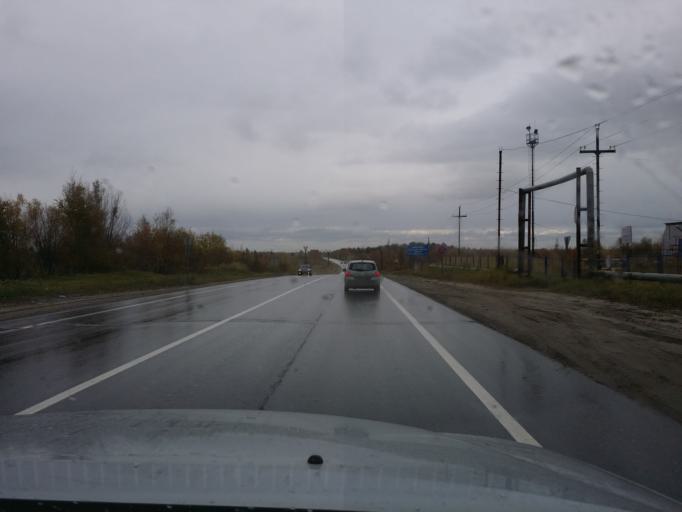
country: RU
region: Khanty-Mansiyskiy Avtonomnyy Okrug
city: Megion
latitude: 61.0550
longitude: 76.1136
